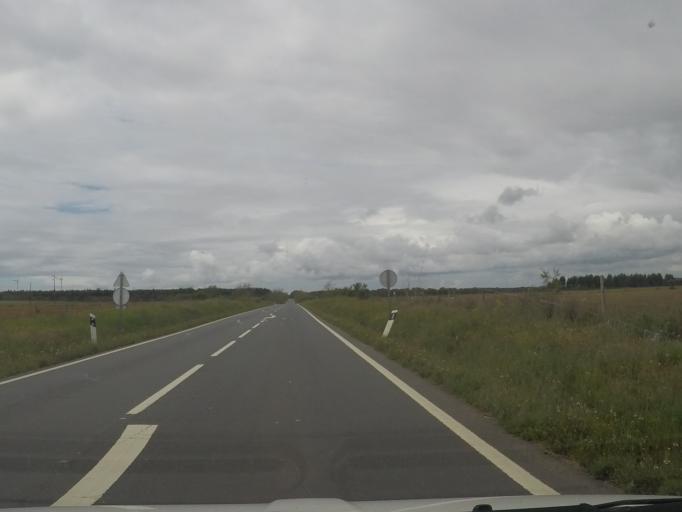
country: PT
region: Setubal
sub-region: Santiago do Cacem
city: Cercal
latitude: 37.8411
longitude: -8.7041
